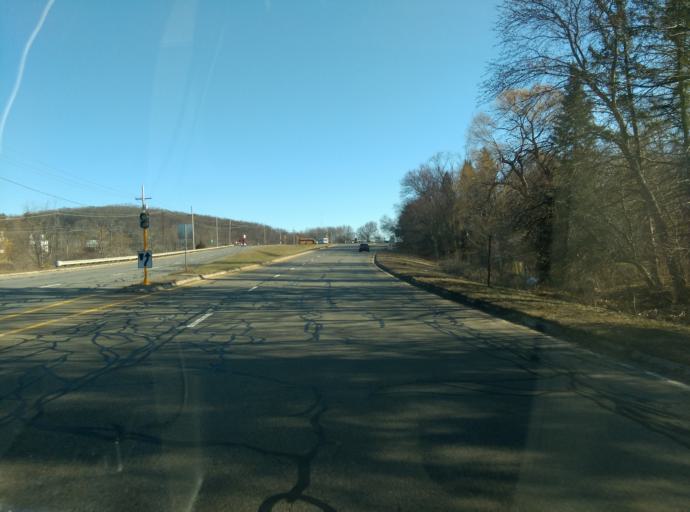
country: US
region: Massachusetts
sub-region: Essex County
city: Haverhill
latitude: 42.7478
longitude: -71.1092
